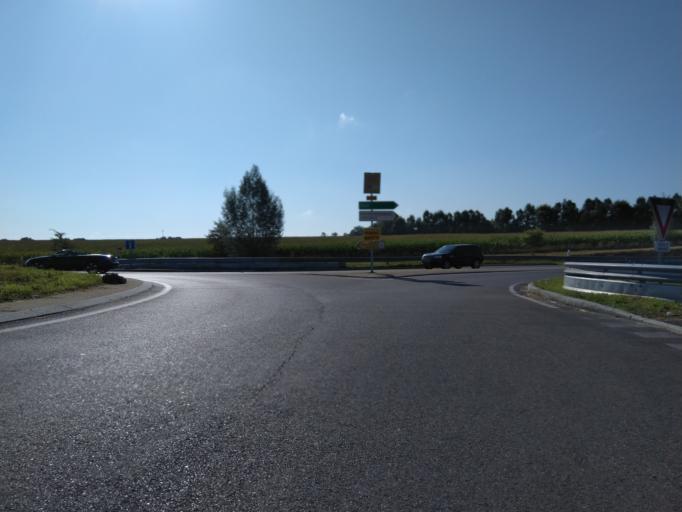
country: FR
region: Aquitaine
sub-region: Departement des Landes
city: Saint-Vincent-de-Paul
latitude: 43.7383
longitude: -1.0168
